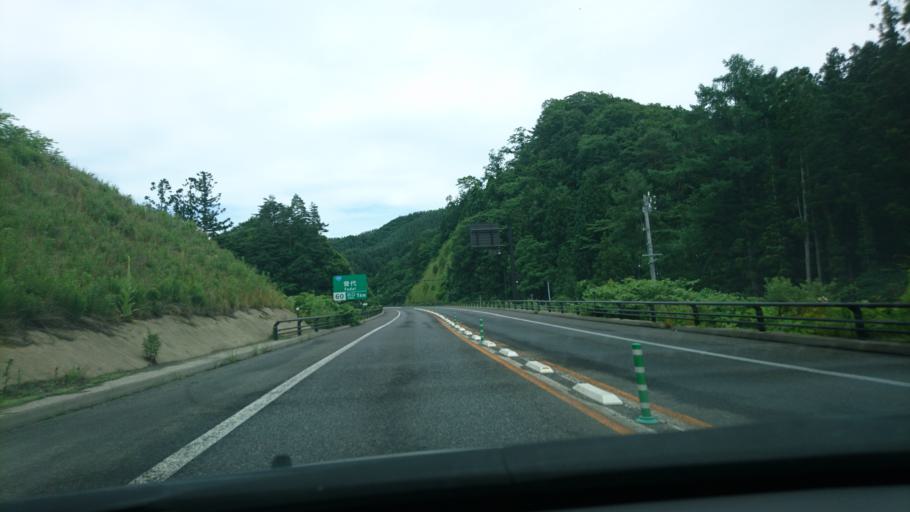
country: JP
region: Iwate
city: Miyako
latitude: 39.9929
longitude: 141.8801
